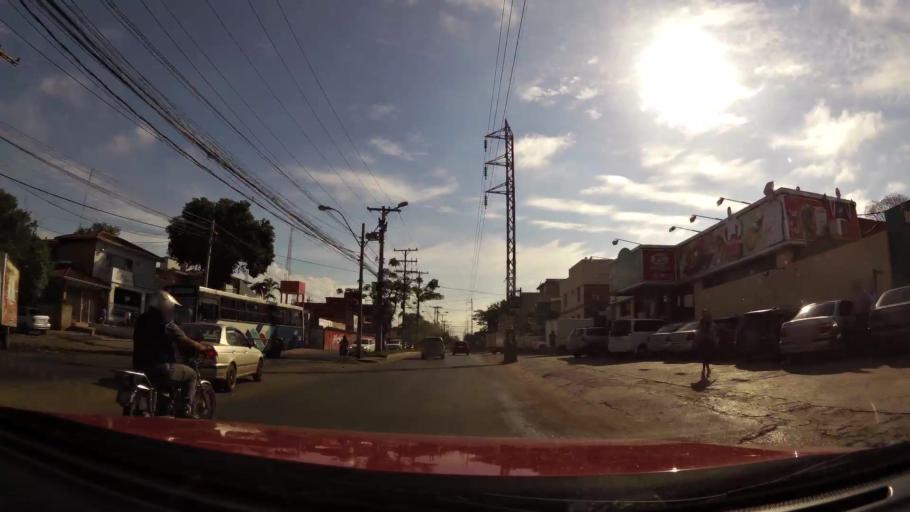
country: PY
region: Asuncion
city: Asuncion
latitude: -25.2704
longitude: -57.6029
